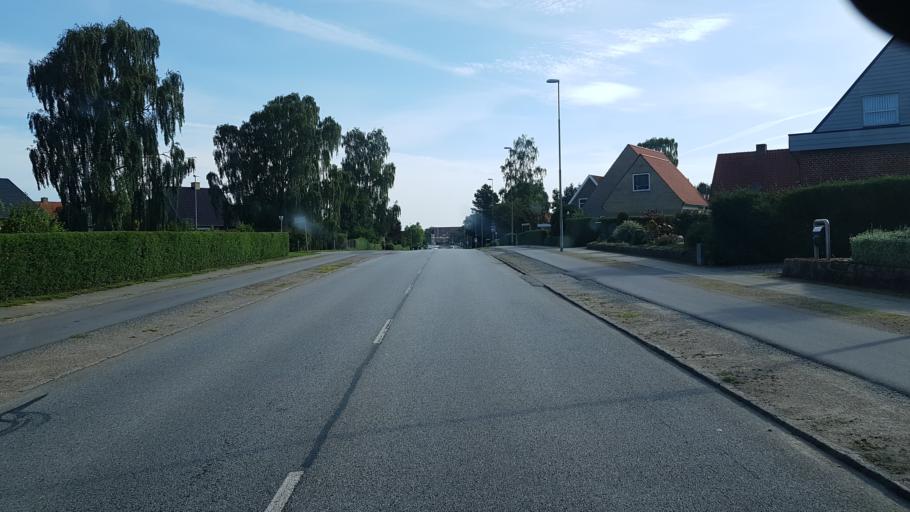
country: DK
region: South Denmark
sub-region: Haderslev Kommune
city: Haderslev
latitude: 55.2411
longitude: 9.4970
